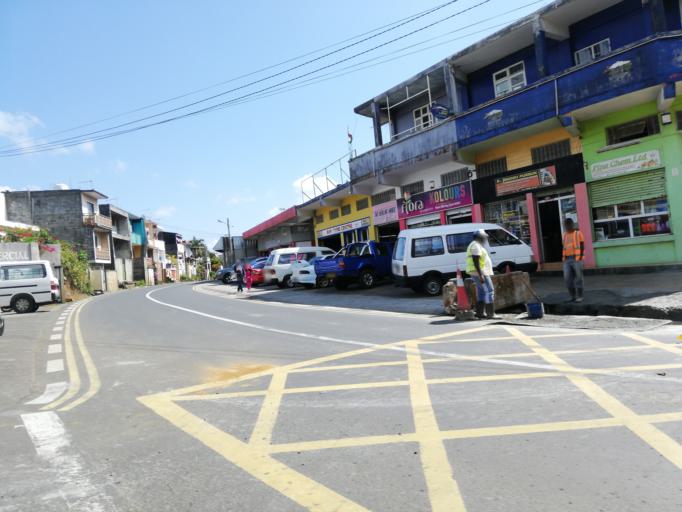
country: MU
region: Moka
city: Verdun
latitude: -20.2238
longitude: 57.5401
